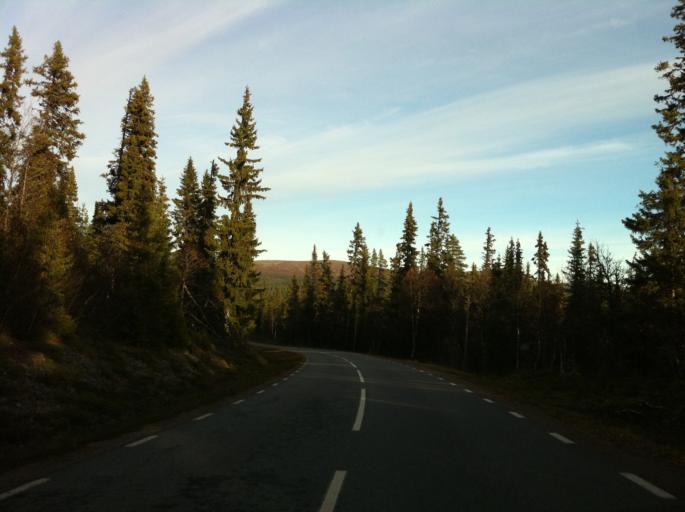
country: NO
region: Hedmark
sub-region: Engerdal
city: Engerdal
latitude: 62.0714
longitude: 12.2038
